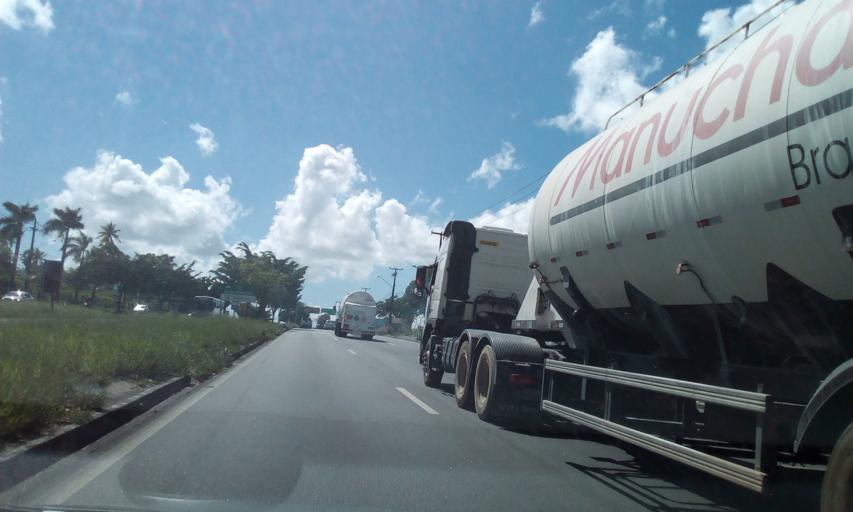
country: BR
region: Pernambuco
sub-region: Igarassu
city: Igarassu
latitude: -7.8545
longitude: -34.9088
